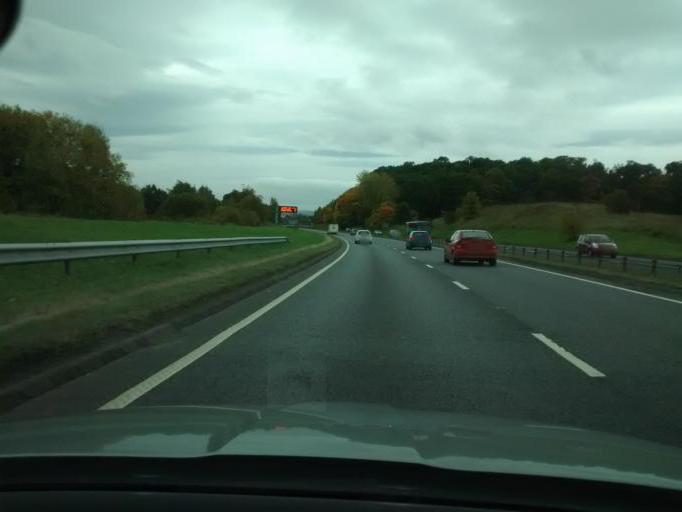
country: GB
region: Scotland
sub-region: Perth and Kinross
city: Luncarty
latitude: 56.4332
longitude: -3.4727
